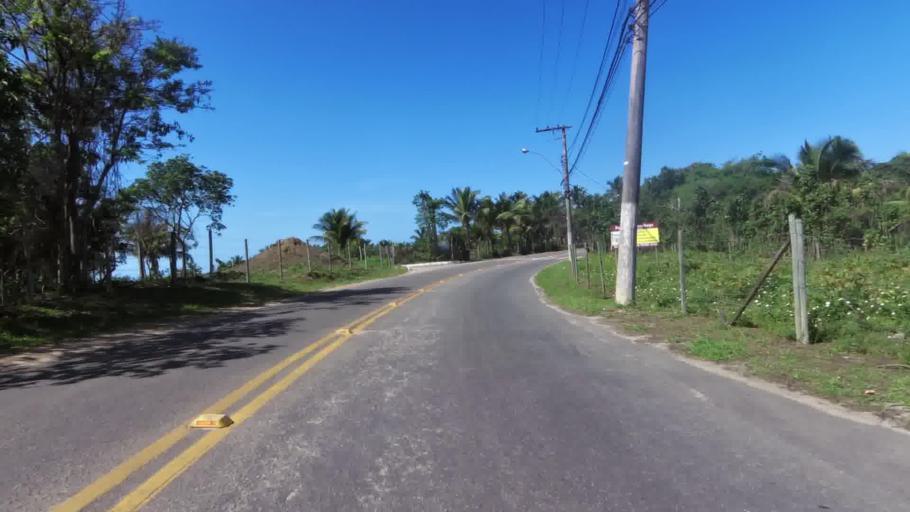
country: BR
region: Espirito Santo
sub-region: Piuma
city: Piuma
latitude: -20.8271
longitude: -40.6253
